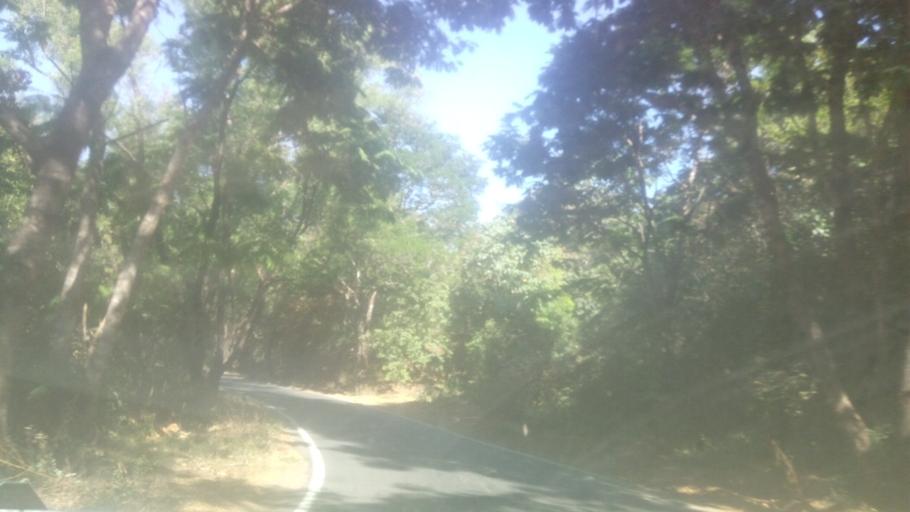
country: IN
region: Goa
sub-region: North Goa
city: Valpoy
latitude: 15.6123
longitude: 74.1171
